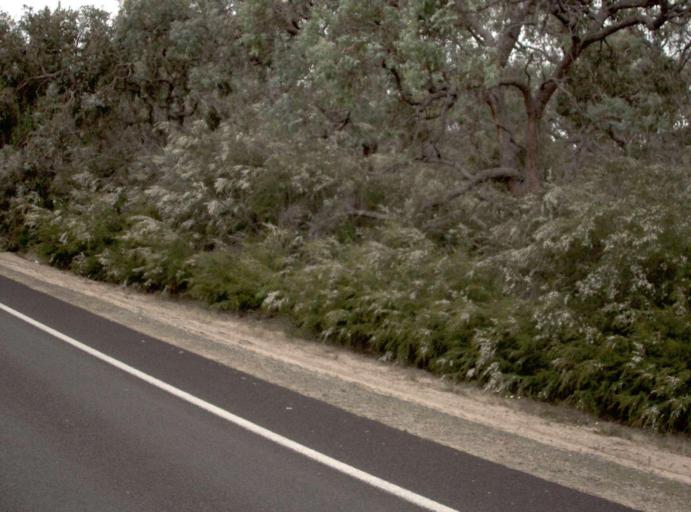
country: AU
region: Victoria
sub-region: Wellington
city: Sale
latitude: -38.3387
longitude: 147.0086
